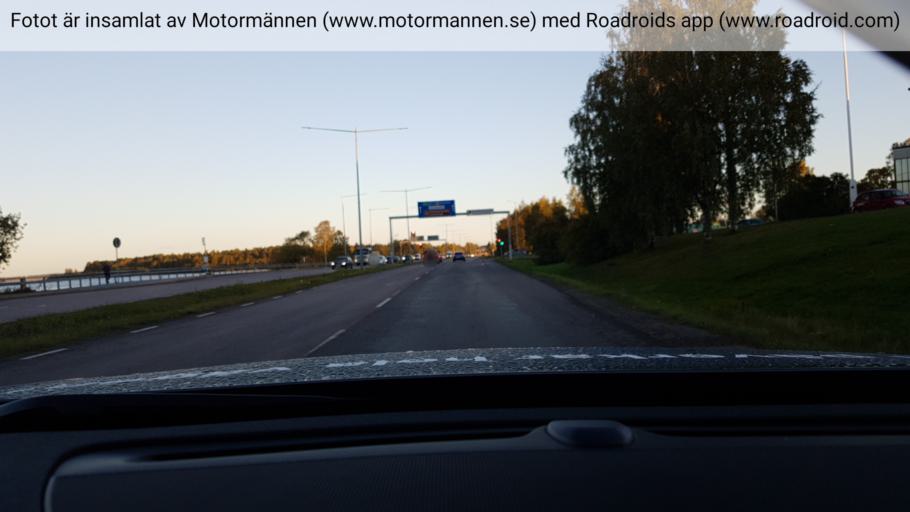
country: SE
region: Norrbotten
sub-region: Lulea Kommun
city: Lulea
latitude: 65.5880
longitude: 22.1485
